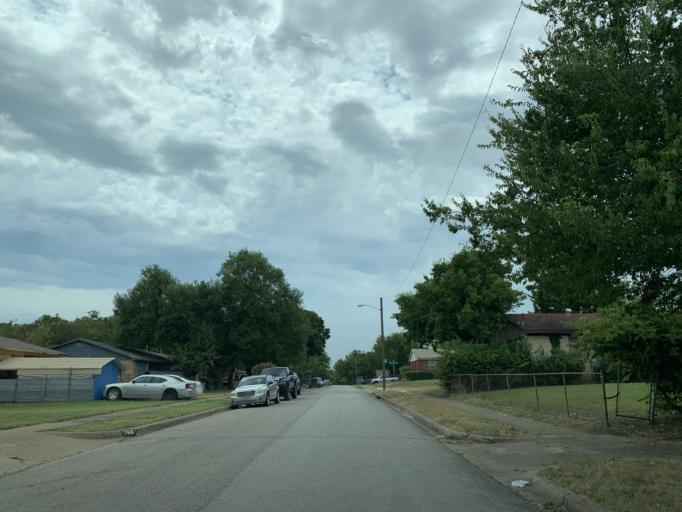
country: US
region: Texas
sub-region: Dallas County
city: DeSoto
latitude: 32.6570
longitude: -96.8319
